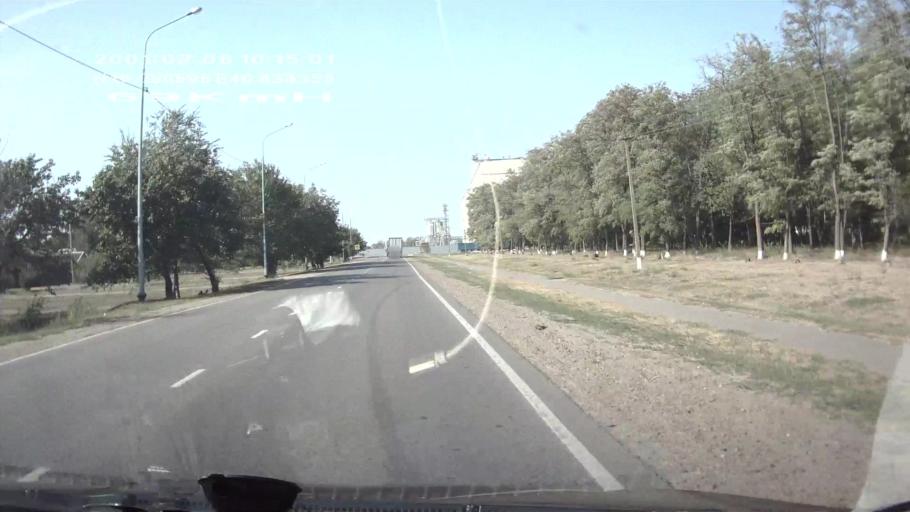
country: RU
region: Krasnodarskiy
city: Belaya Glina
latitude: 46.0906
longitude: 40.8331
